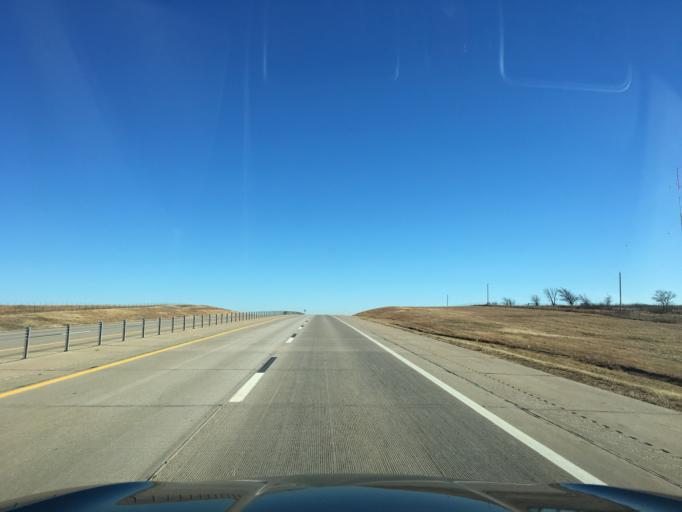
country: US
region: Oklahoma
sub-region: Noble County
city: Perry
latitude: 36.3920
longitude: -97.1542
